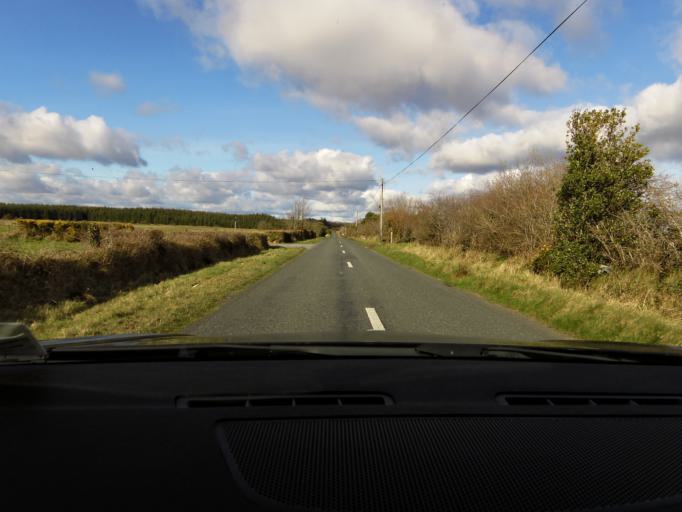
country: IE
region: Connaught
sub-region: County Galway
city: Athenry
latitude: 53.4491
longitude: -8.5549
